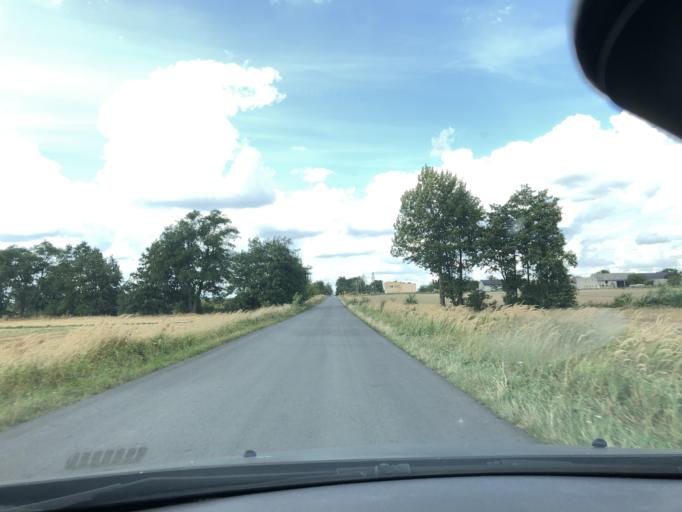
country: PL
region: Lodz Voivodeship
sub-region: Powiat wieruszowski
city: Walichnowy
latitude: 51.2440
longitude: 18.3888
